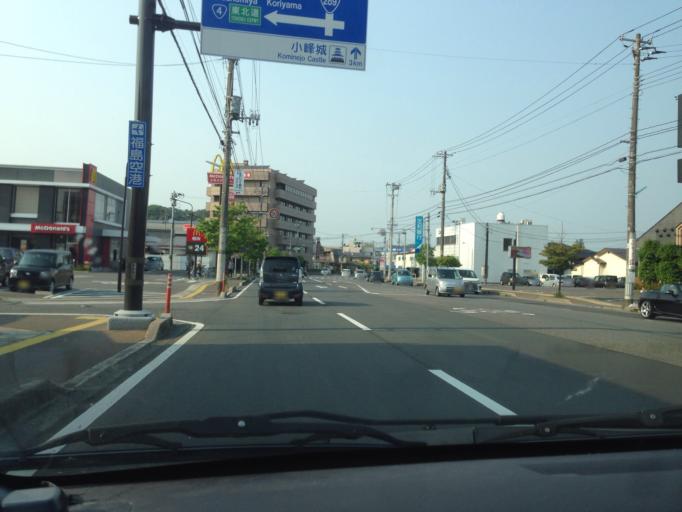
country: JP
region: Tochigi
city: Kuroiso
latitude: 37.1219
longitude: 140.1947
